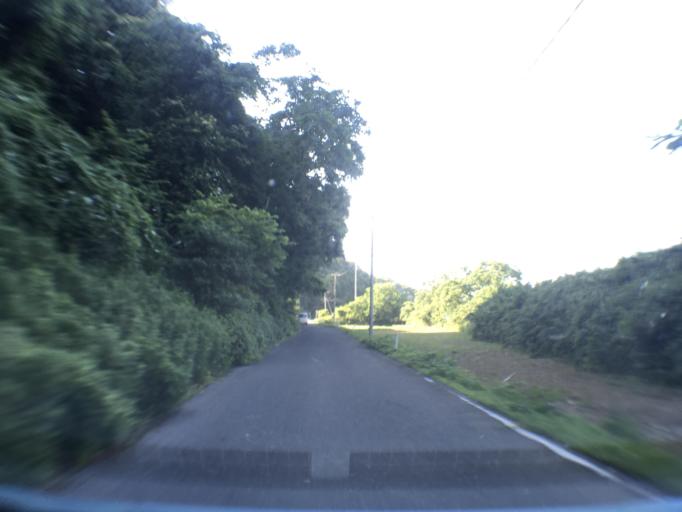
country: JP
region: Miyagi
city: Wakuya
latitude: 38.6332
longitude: 141.2855
